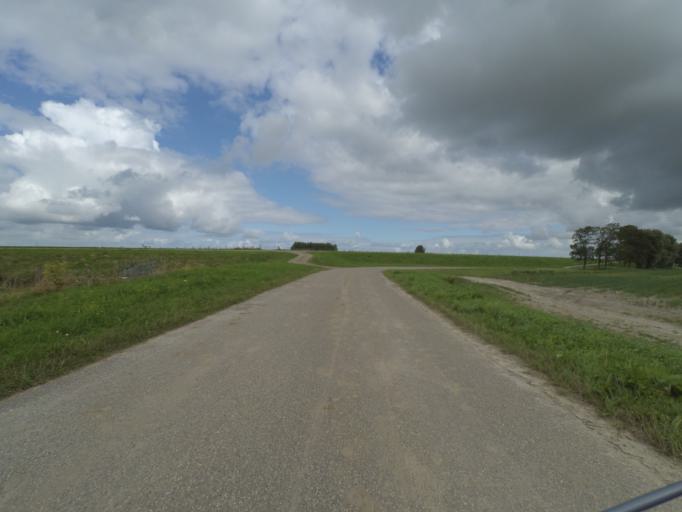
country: NL
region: Groningen
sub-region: Gemeente Zuidhorn
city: Grijpskerk
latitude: 53.3125
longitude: 6.2628
